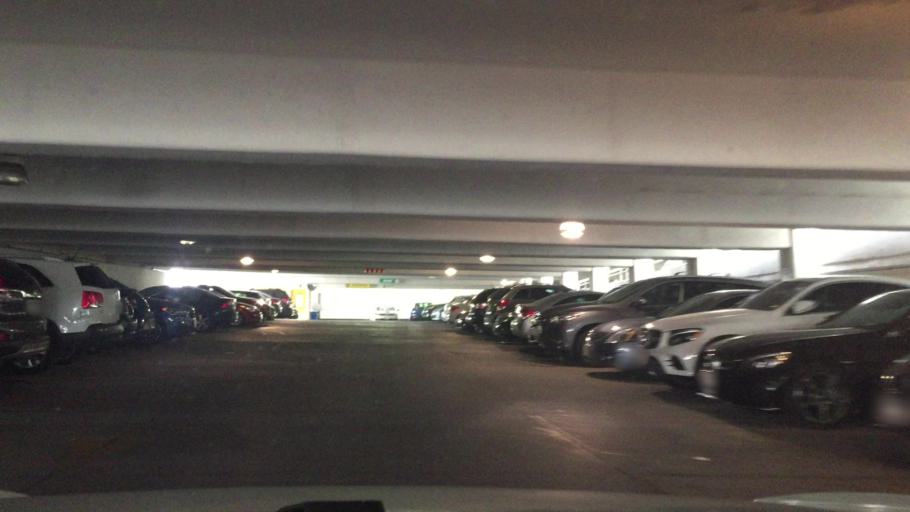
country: CA
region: Ontario
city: Concord
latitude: 43.7749
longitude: -79.5014
